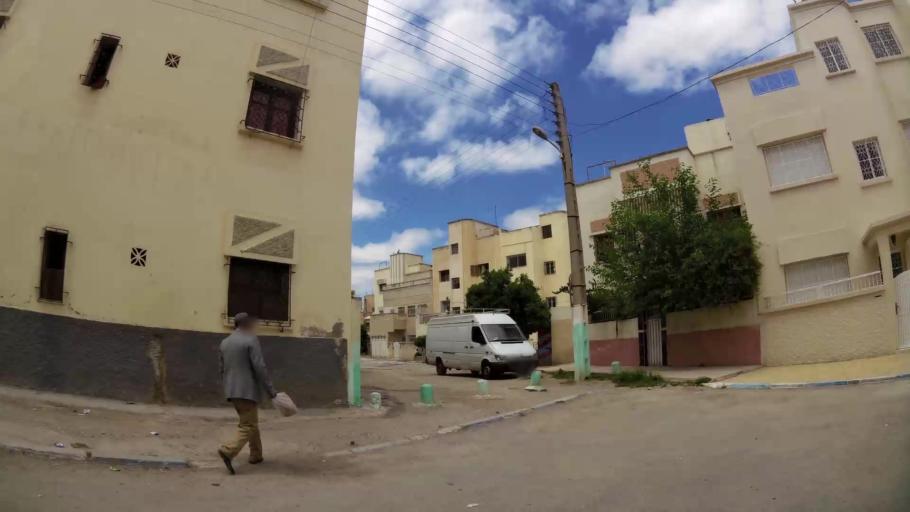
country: MA
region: Fes-Boulemane
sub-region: Fes
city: Fes
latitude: 34.0380
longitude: -5.0208
